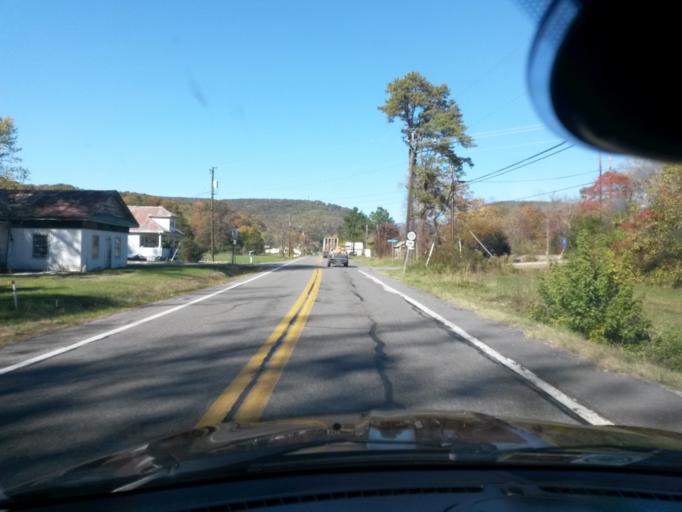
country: US
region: Virginia
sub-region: Alleghany County
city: Clifton Forge
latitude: 37.7878
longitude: -79.7817
